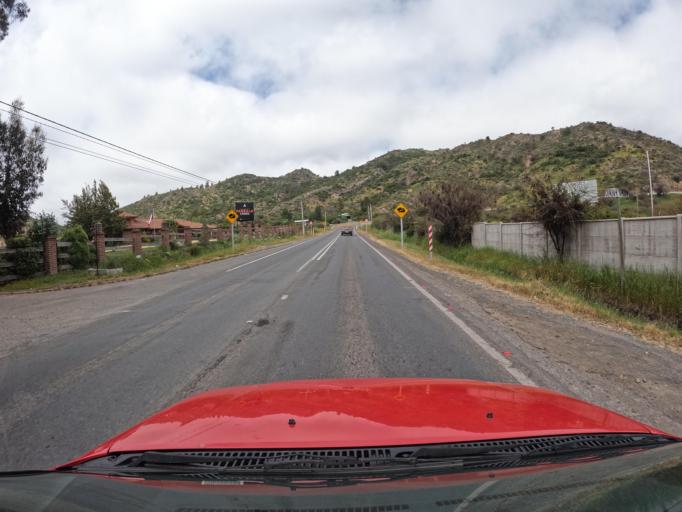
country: CL
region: O'Higgins
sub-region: Provincia de Colchagua
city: Santa Cruz
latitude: -34.6606
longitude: -71.4111
